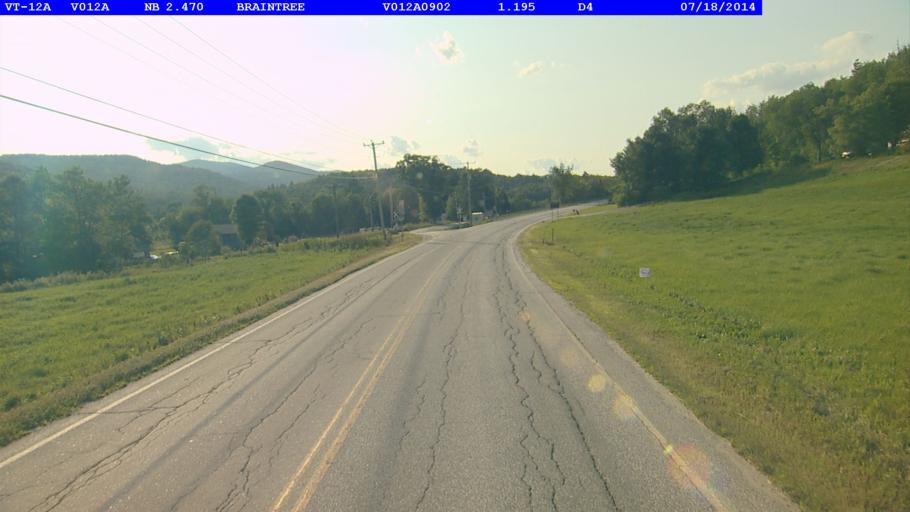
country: US
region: Vermont
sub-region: Orange County
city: Randolph
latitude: 43.9390
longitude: -72.7061
